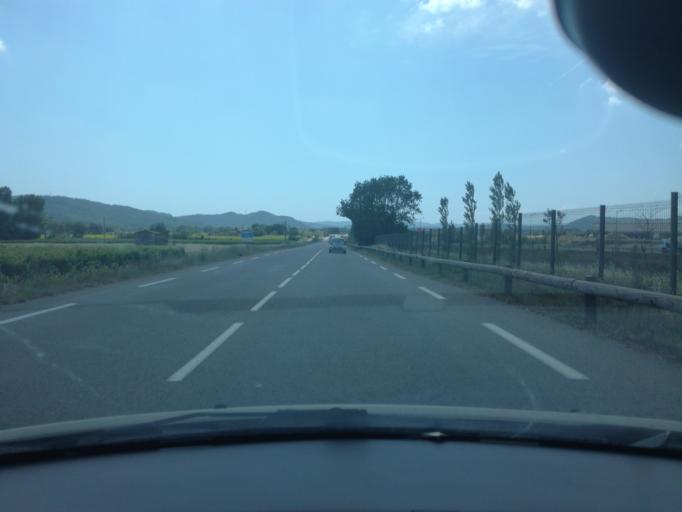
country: FR
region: Provence-Alpes-Cote d'Azur
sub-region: Departement du Var
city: Les Arcs
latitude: 43.4524
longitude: 6.5010
